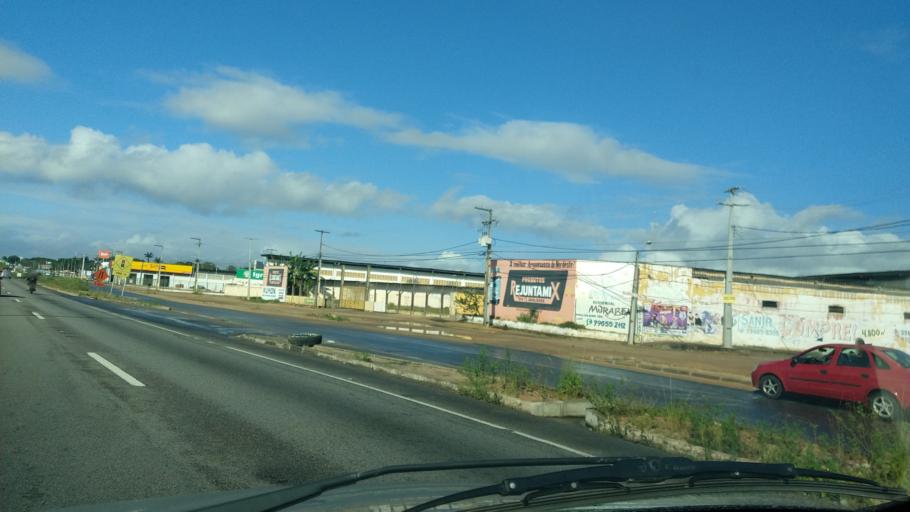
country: BR
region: Rio Grande do Norte
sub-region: Parnamirim
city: Parnamirim
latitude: -5.8986
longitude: -35.2589
